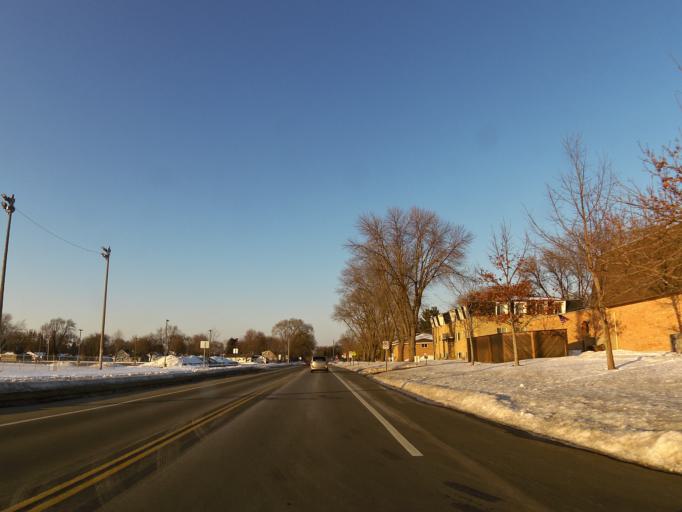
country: US
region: Minnesota
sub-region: Scott County
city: Shakopee
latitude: 44.7865
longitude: -93.5201
